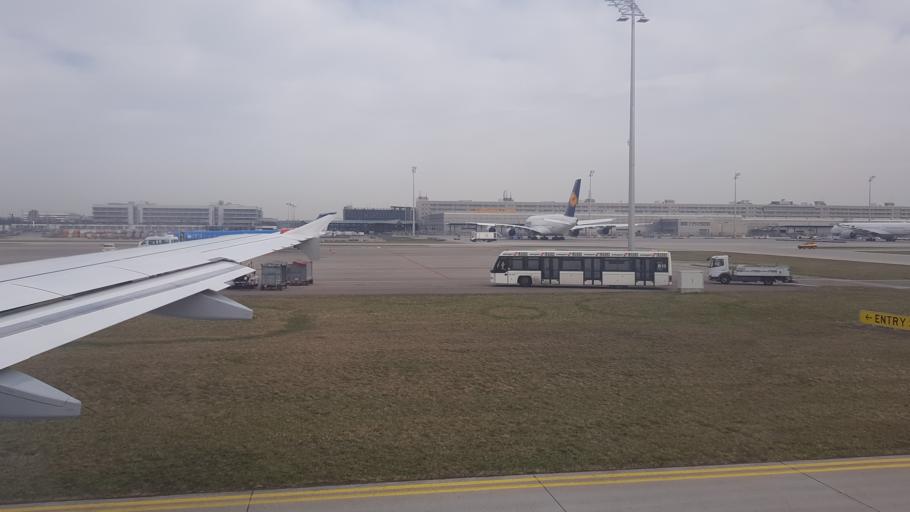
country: DE
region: Bavaria
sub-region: Upper Bavaria
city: Hallbergmoos
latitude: 48.3454
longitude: 11.7656
